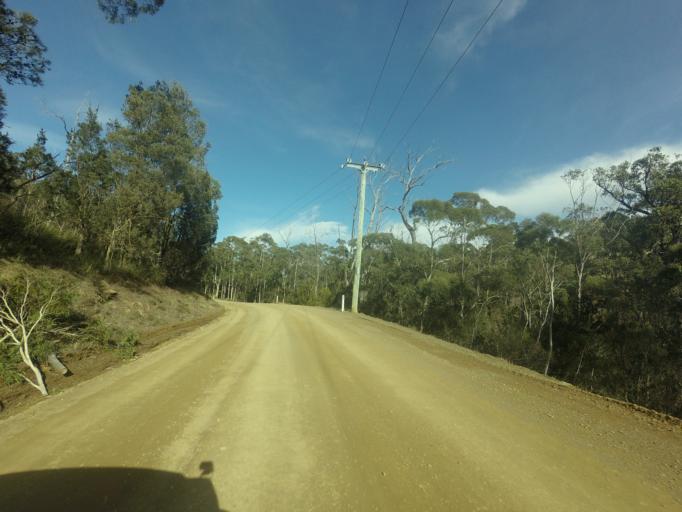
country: AU
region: Tasmania
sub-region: Huon Valley
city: Huonville
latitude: -43.0595
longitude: 147.0950
